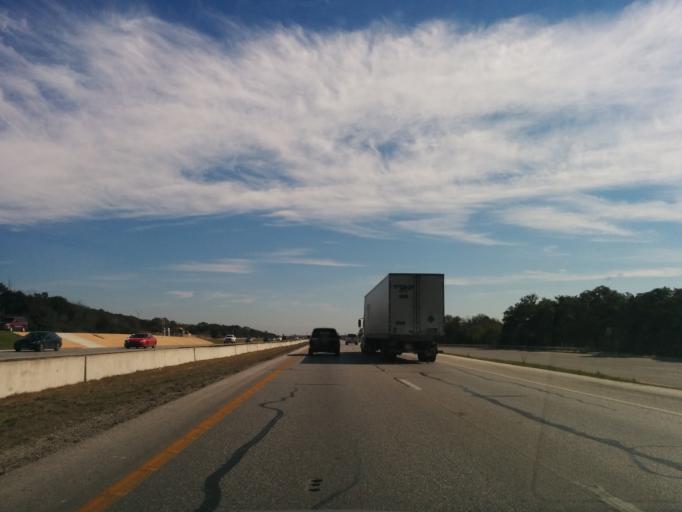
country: US
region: Texas
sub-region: Bexar County
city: Shavano Park
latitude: 29.6010
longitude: -98.5584
